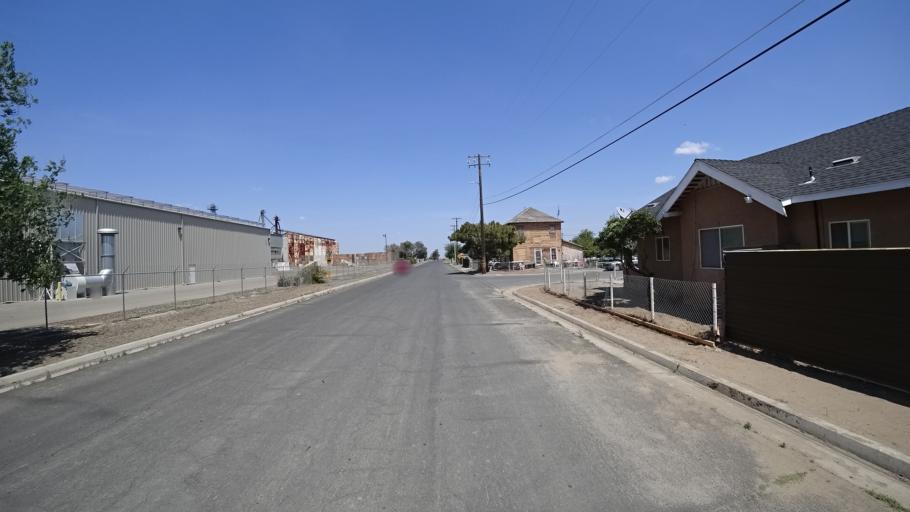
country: US
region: California
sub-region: Kings County
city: Stratford
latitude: 36.1903
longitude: -119.8244
